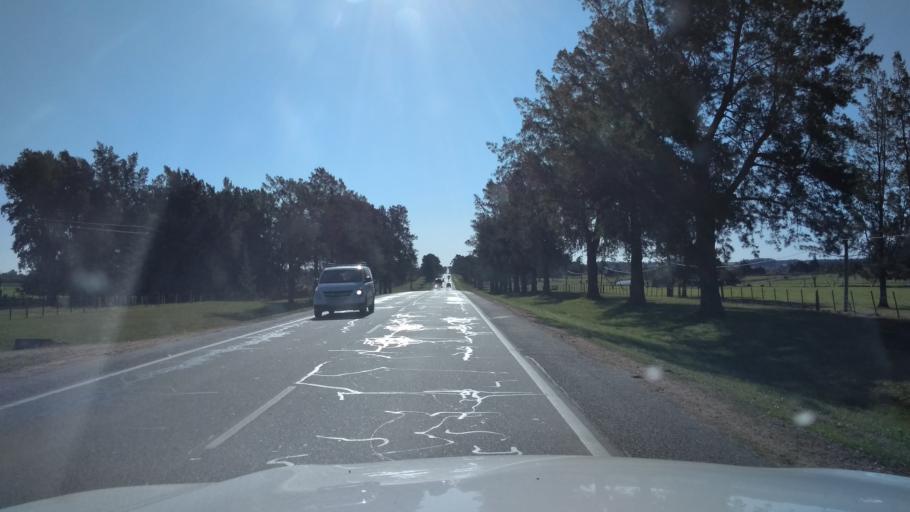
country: UY
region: Canelones
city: San Jacinto
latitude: -34.5838
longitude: -55.8416
